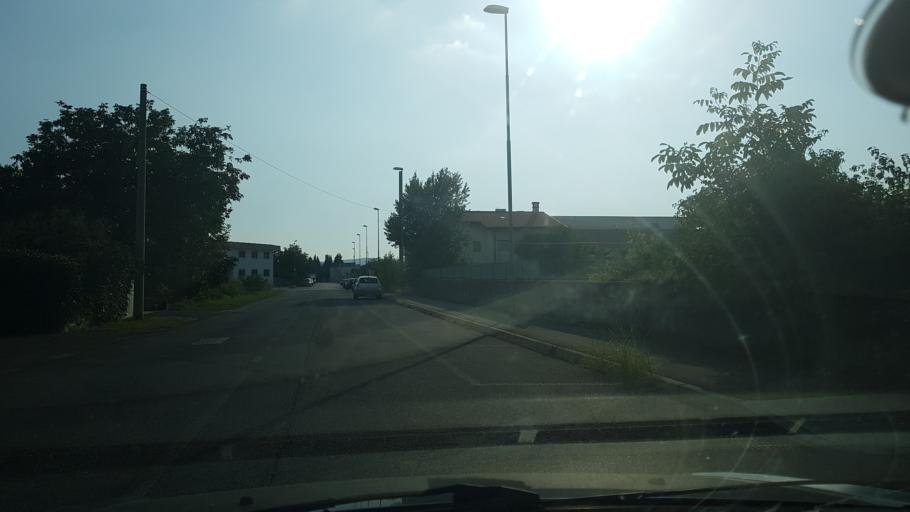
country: IT
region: Friuli Venezia Giulia
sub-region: Provincia di Gorizia
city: Gorizia
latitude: 45.9254
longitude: 13.6201
